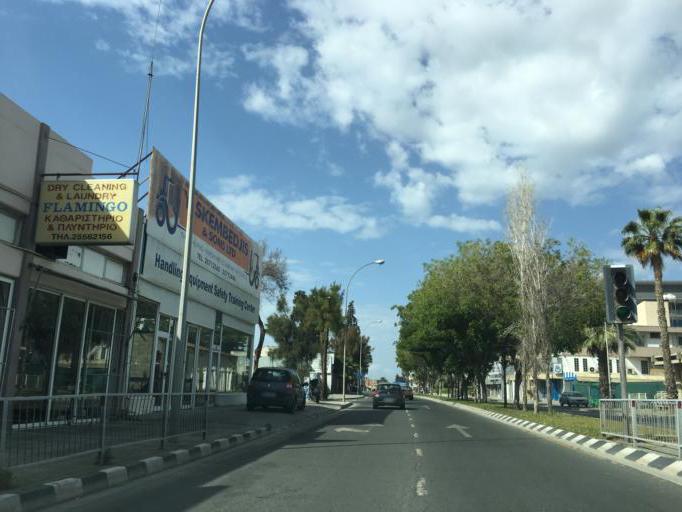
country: CY
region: Limassol
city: Limassol
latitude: 34.6642
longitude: 33.0194
